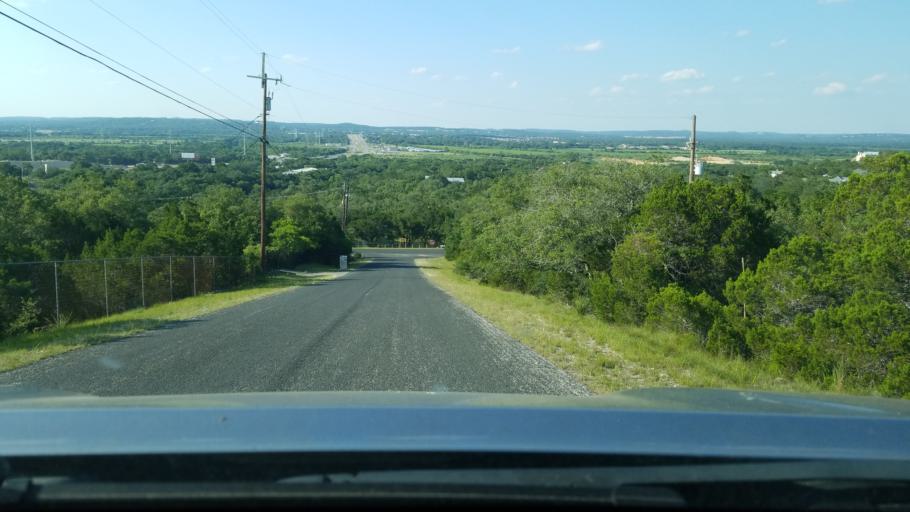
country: US
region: Texas
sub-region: Bexar County
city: Timberwood Park
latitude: 29.7098
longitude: -98.4455
